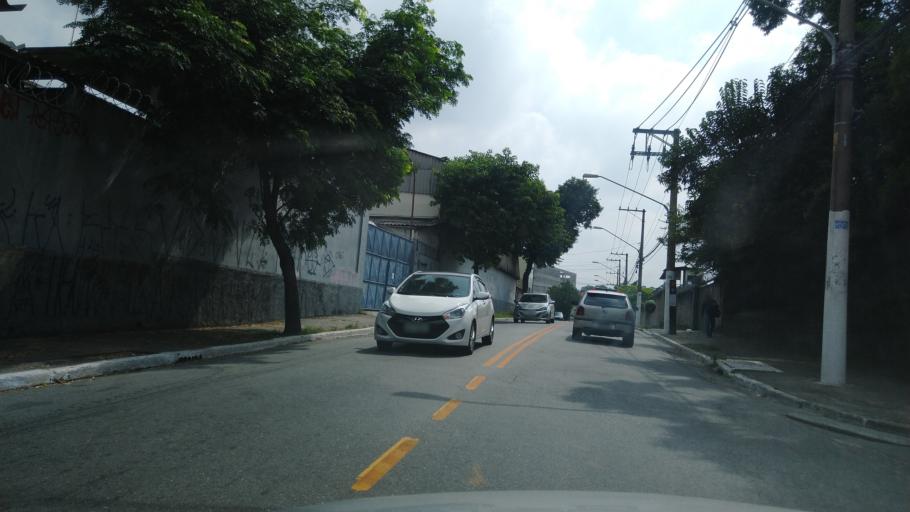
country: BR
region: Sao Paulo
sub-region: Guarulhos
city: Guarulhos
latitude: -23.4719
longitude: -46.5766
